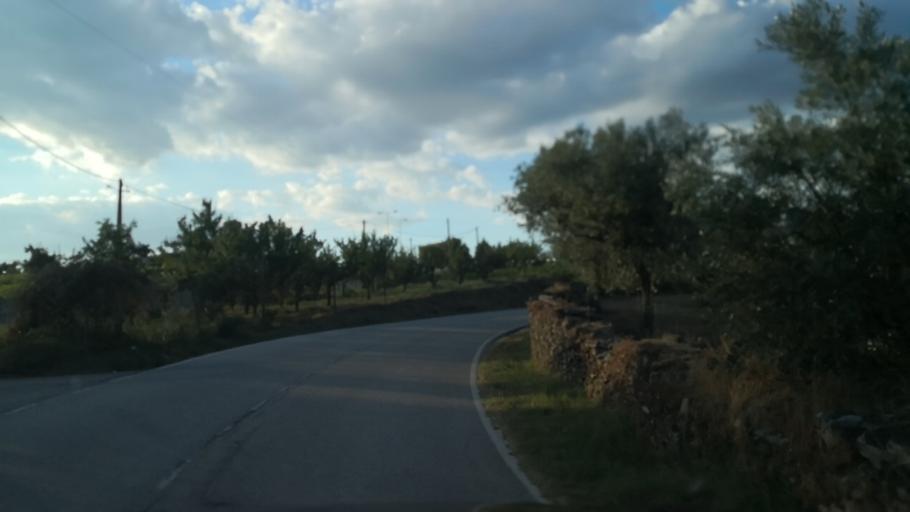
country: PT
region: Vila Real
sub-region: Sabrosa
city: Sabrosa
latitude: 41.2729
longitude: -7.4604
